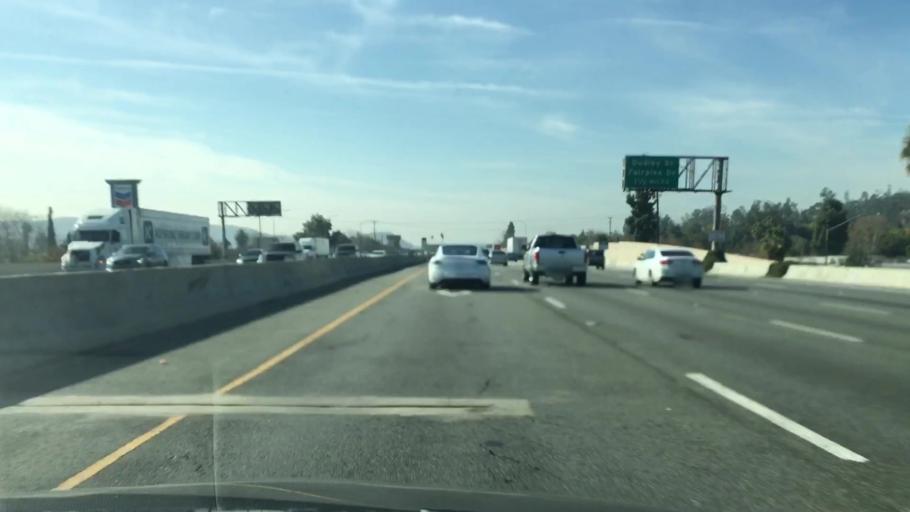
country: US
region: California
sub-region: Los Angeles County
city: Pomona
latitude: 34.0741
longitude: -117.7520
